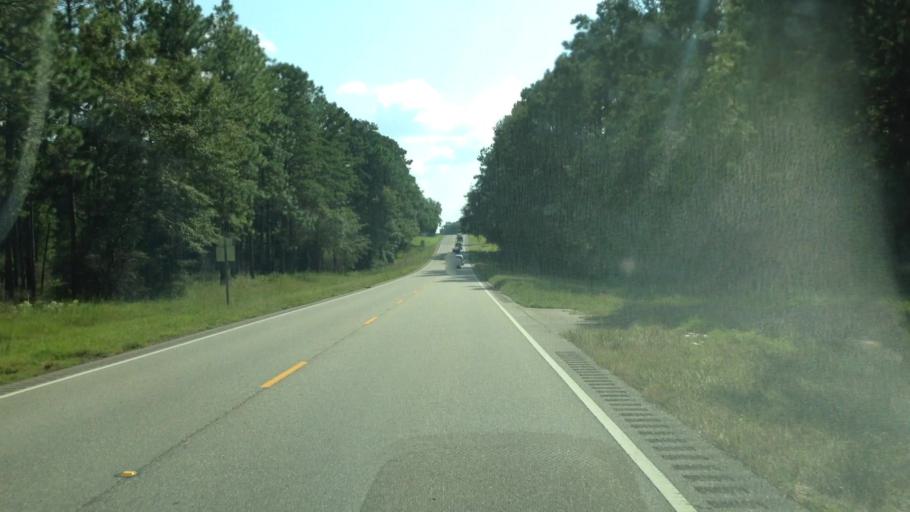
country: US
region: Florida
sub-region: Okaloosa County
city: Crestview
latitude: 30.9974
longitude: -86.6270
